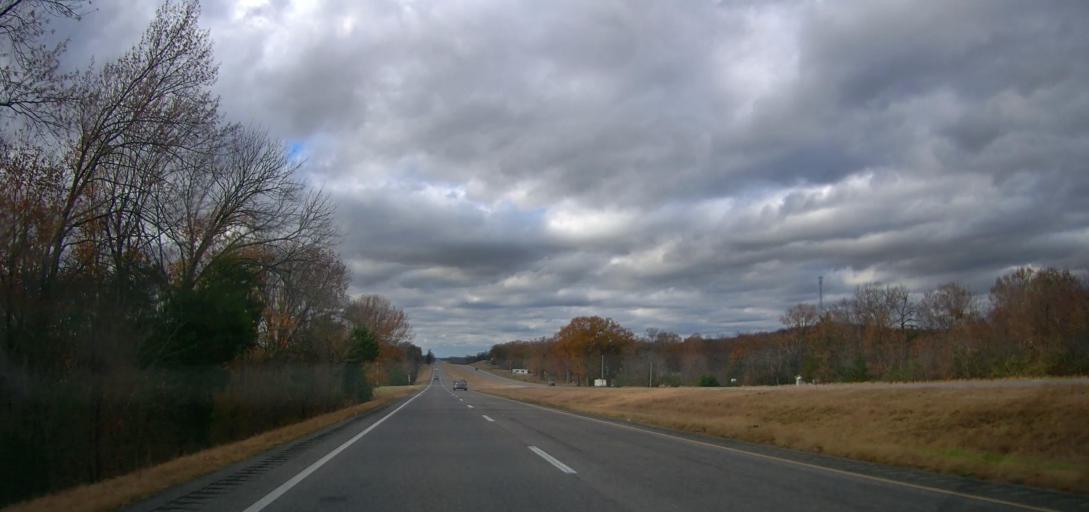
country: US
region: Alabama
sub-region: Morgan County
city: Danville
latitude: 34.3985
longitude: -87.1284
